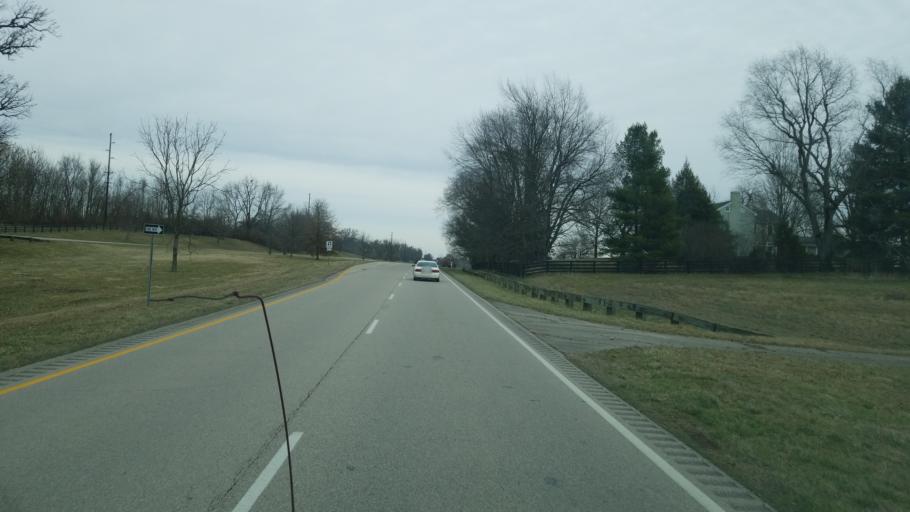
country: US
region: Kentucky
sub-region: Bourbon County
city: Paris
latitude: 38.1793
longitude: -84.2999
